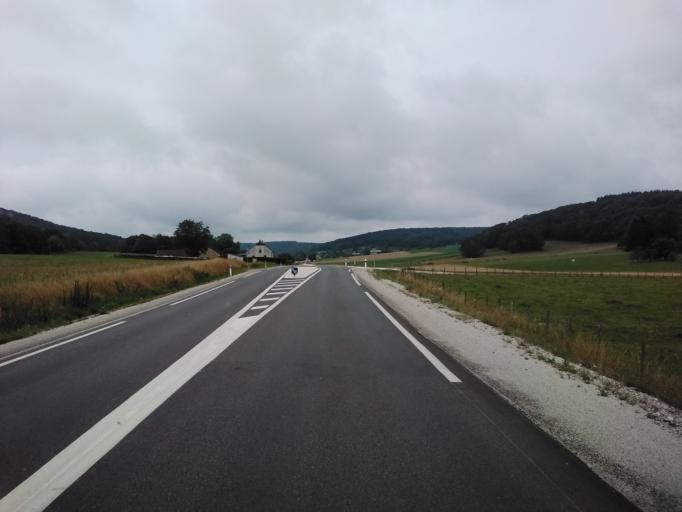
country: FR
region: Franche-Comte
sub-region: Departement de la Haute-Saone
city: Rioz
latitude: 47.4857
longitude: 6.1035
